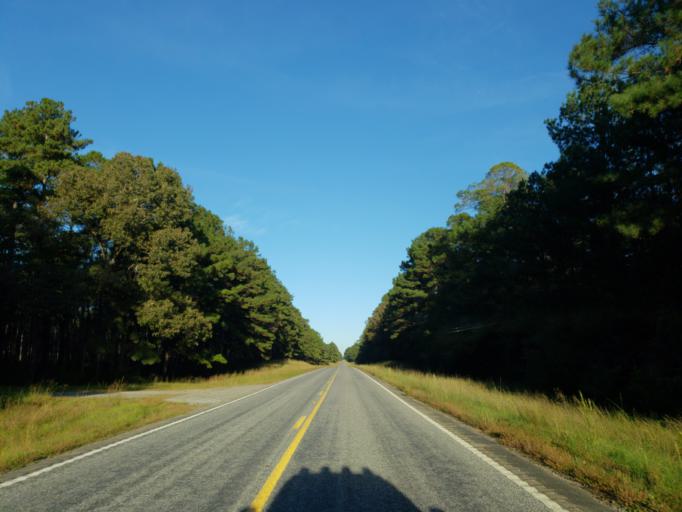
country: US
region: Mississippi
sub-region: Wayne County
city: Belmont
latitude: 31.3970
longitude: -88.6455
